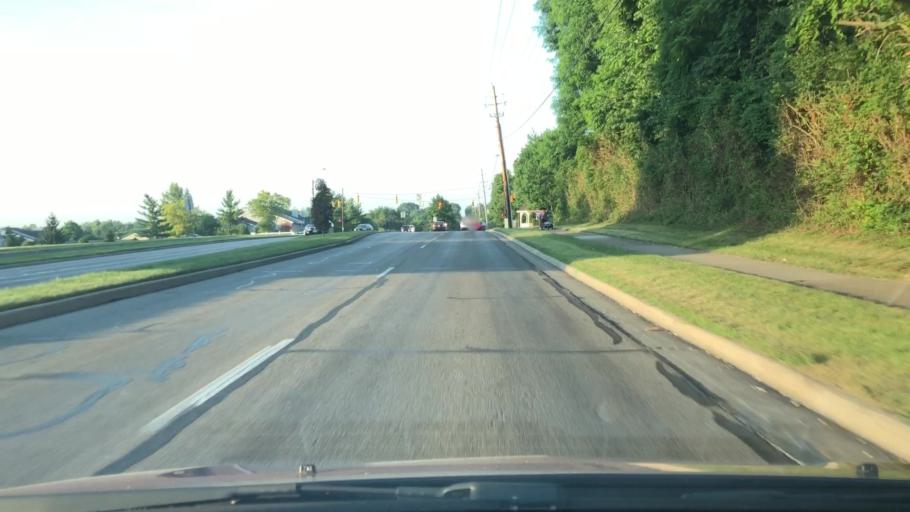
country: US
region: Ohio
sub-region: Montgomery County
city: Centerville
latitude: 39.6504
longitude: -84.1278
